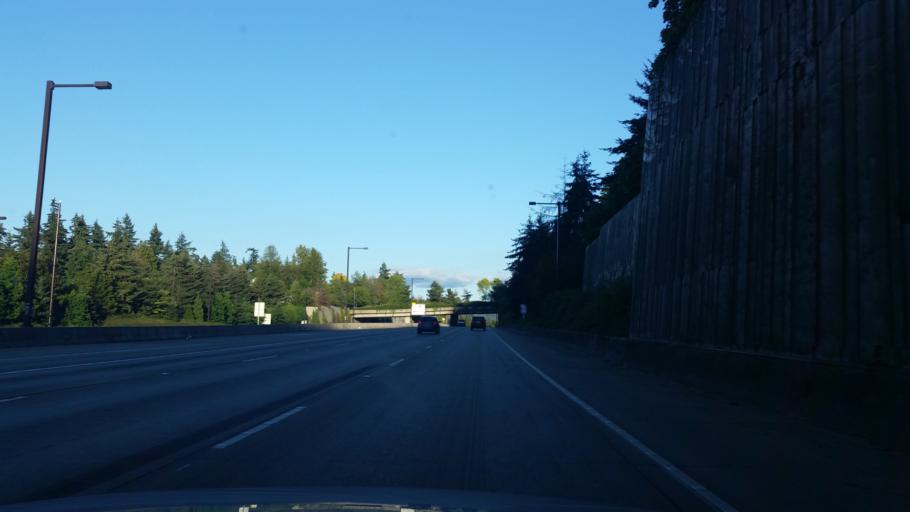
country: US
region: Washington
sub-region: King County
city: Mercer Island
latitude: 47.5835
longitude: -122.2230
